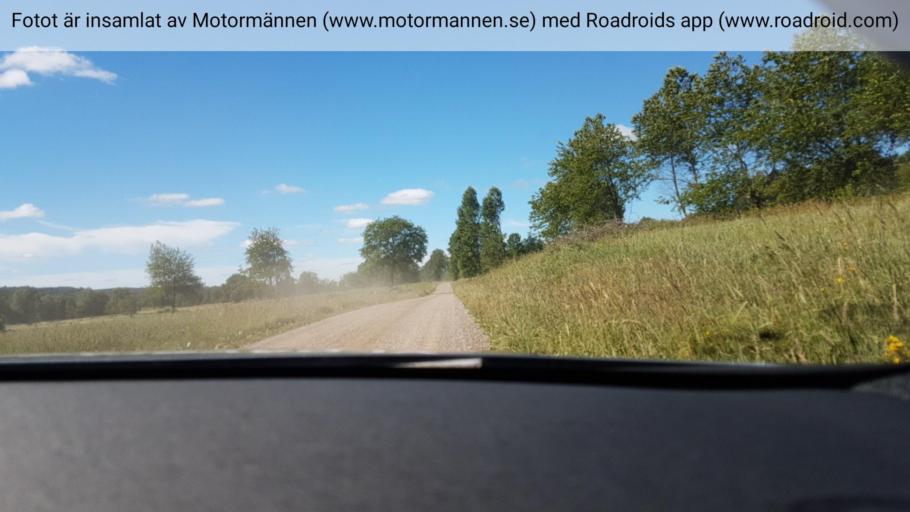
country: SE
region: Vaestra Goetaland
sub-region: Falkopings Kommun
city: Akarp
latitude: 58.2177
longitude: 13.7644
